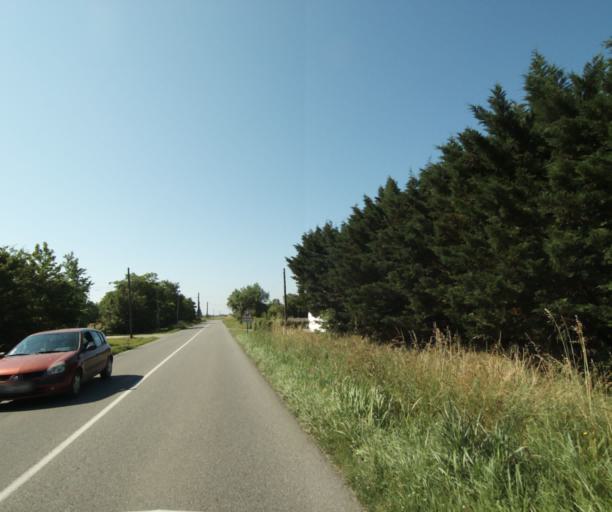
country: FR
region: Midi-Pyrenees
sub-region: Departement du Tarn-et-Garonne
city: Bressols
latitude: 43.9681
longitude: 1.3578
